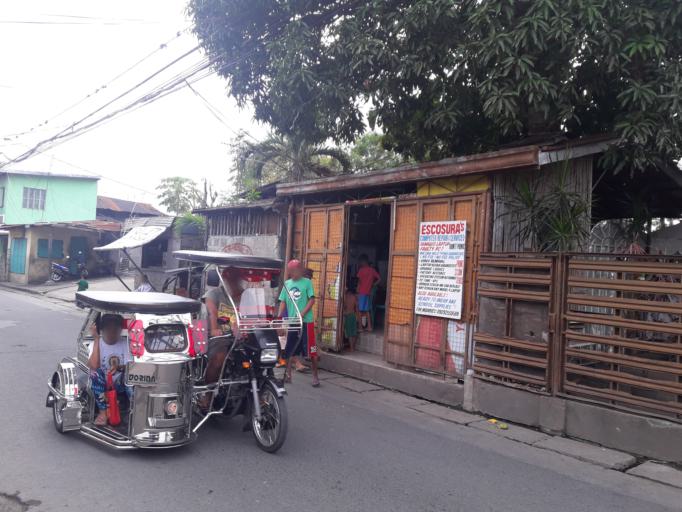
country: PH
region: Calabarzon
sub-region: Province of Laguna
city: Santa Rosa
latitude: 14.3063
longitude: 121.1244
